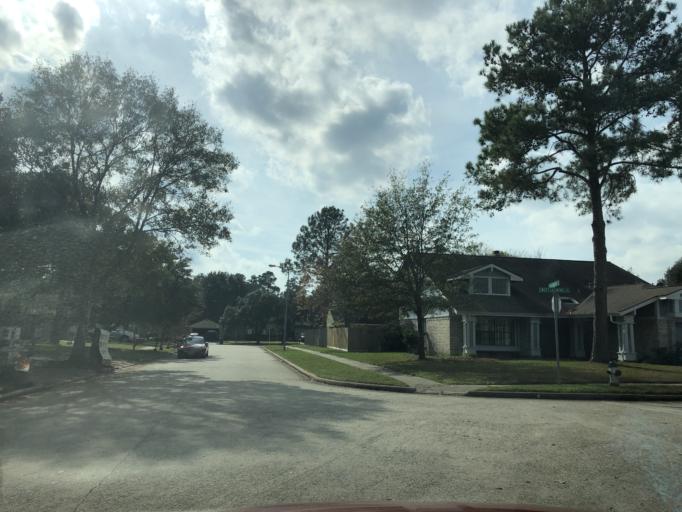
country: US
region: Texas
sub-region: Harris County
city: Tomball
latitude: 30.0371
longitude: -95.5423
